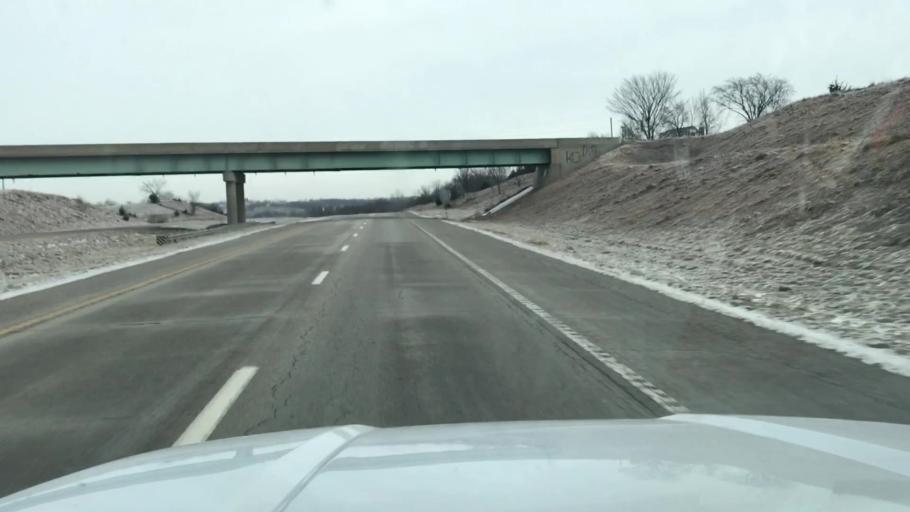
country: US
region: Missouri
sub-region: Andrew County
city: Savannah
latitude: 39.8984
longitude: -94.8570
